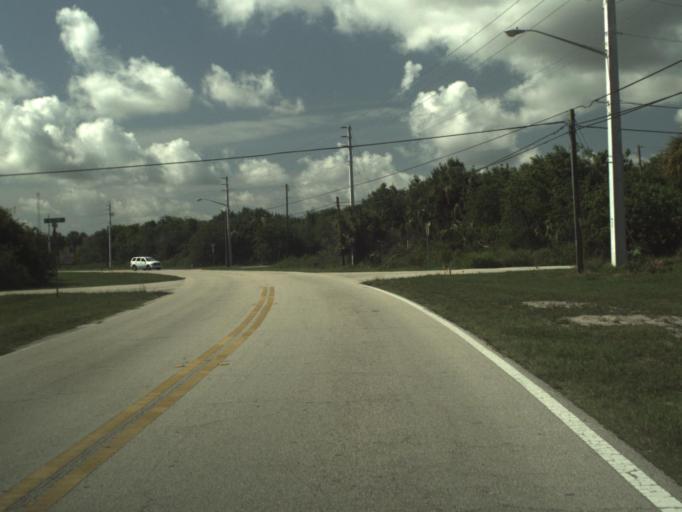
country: US
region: Florida
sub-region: Saint Lucie County
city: Port Saint Lucie
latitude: 27.2333
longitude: -80.3770
